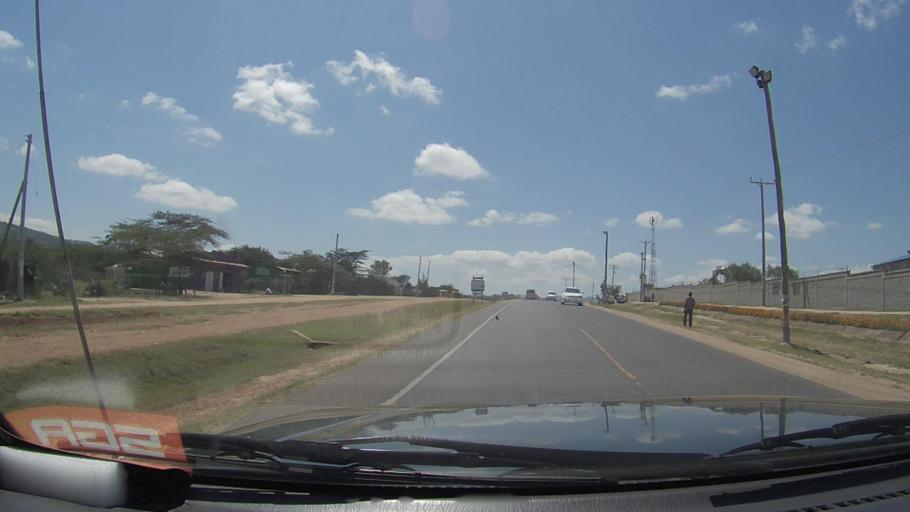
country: KE
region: Machakos
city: Machakos
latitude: -1.5335
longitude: 37.1956
